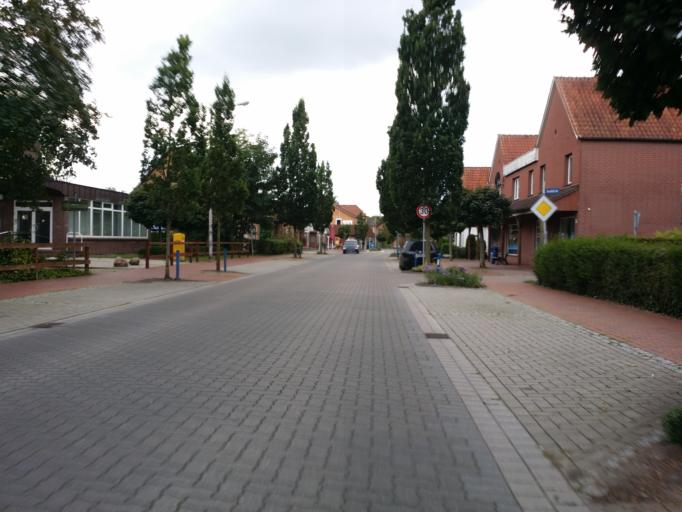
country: DE
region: Lower Saxony
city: Hemmoor
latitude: 53.6854
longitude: 9.1696
